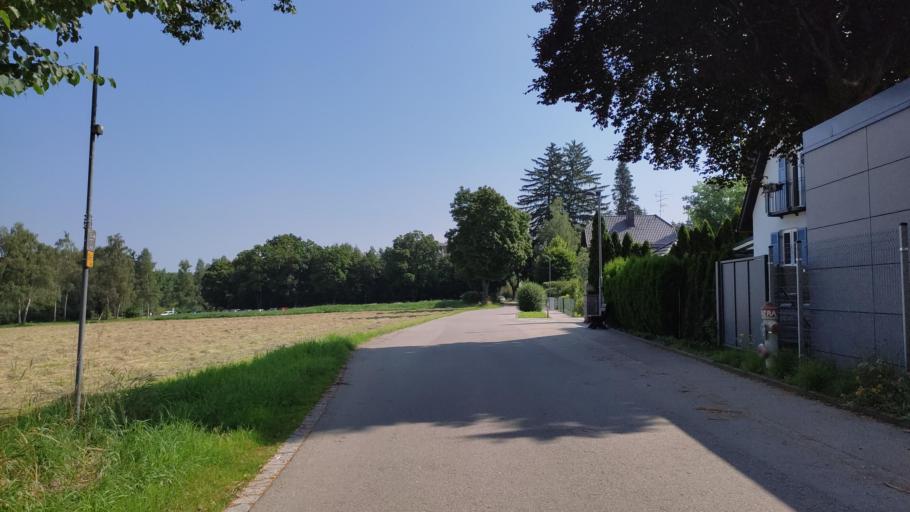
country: DE
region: Bavaria
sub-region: Swabia
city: Bad Worishofen
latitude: 48.0002
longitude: 10.5816
